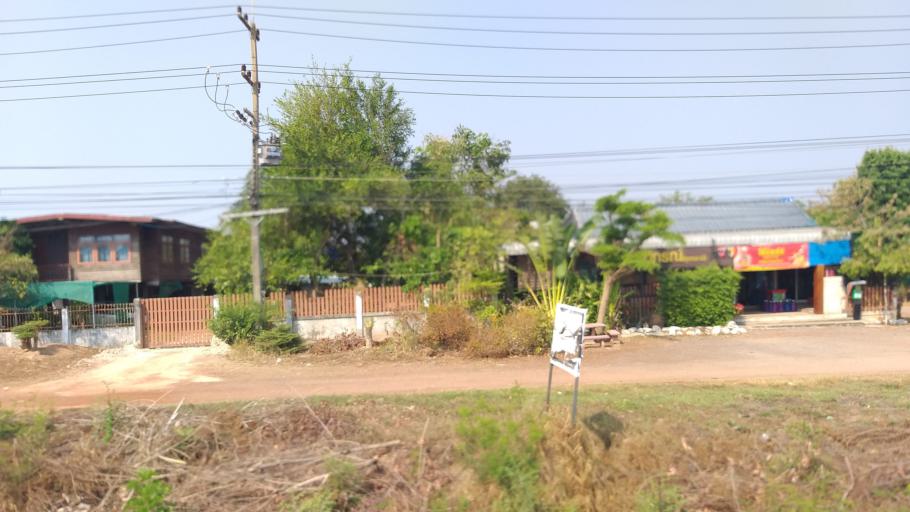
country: TH
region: Changwat Udon Thani
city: Nong Han
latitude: 17.3629
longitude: 103.1450
